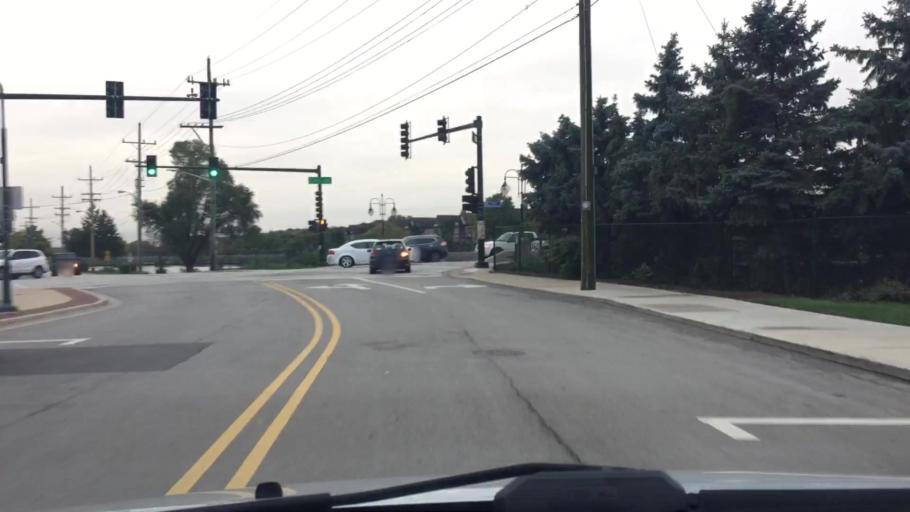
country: US
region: Illinois
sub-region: Kane County
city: Saint Charles
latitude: 41.9128
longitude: -88.3122
